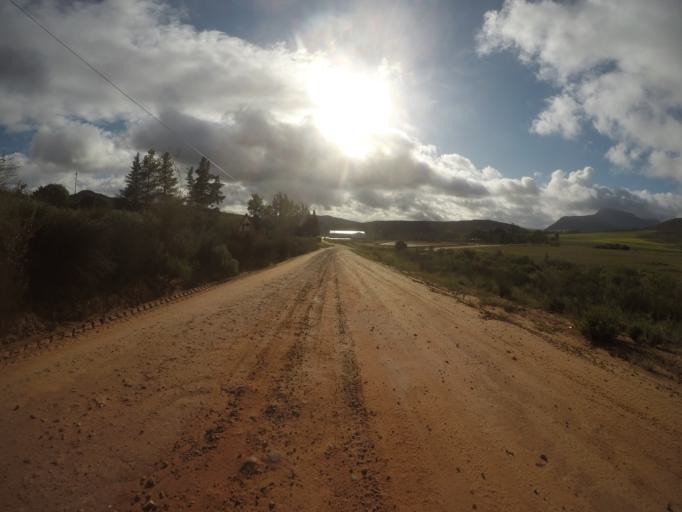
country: ZA
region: Western Cape
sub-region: West Coast District Municipality
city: Clanwilliam
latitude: -32.3423
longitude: 18.8307
